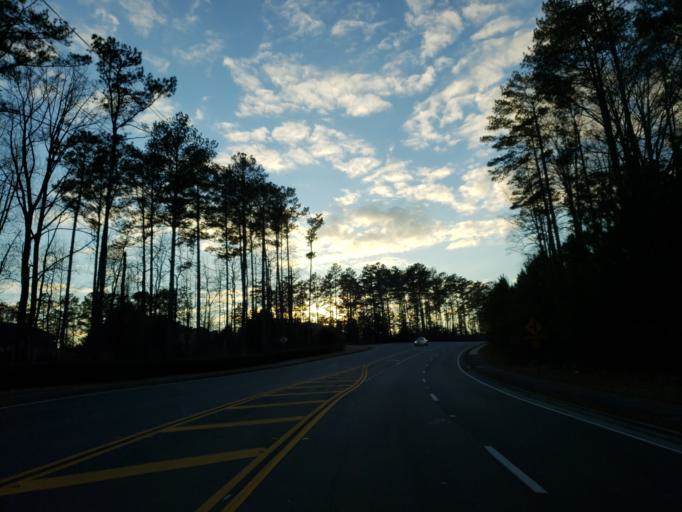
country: US
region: Georgia
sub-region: Cobb County
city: Acworth
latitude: 33.9947
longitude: -84.6958
